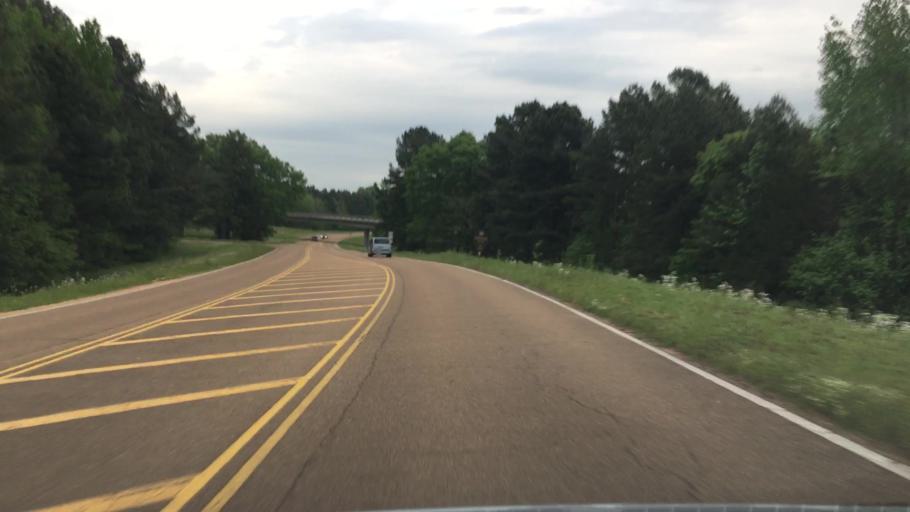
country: US
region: Mississippi
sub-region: Hinds County
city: Clinton
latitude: 32.3830
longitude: -90.2586
